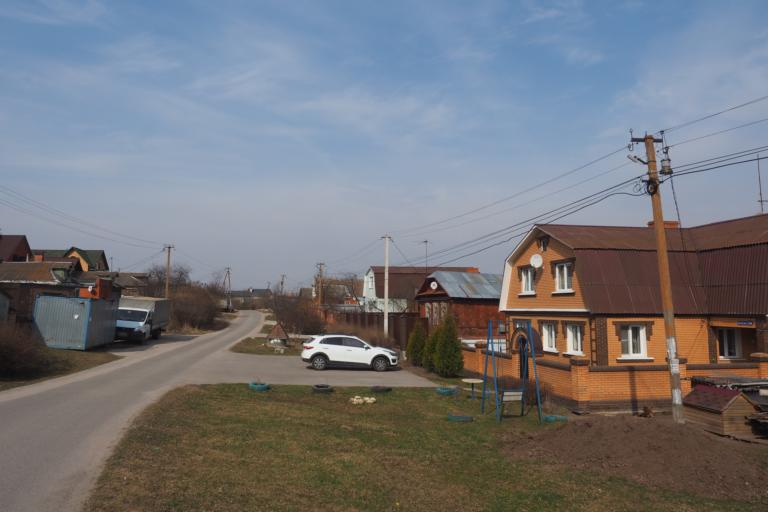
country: RU
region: Moskovskaya
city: Voskresensk
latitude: 55.3396
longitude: 38.6222
